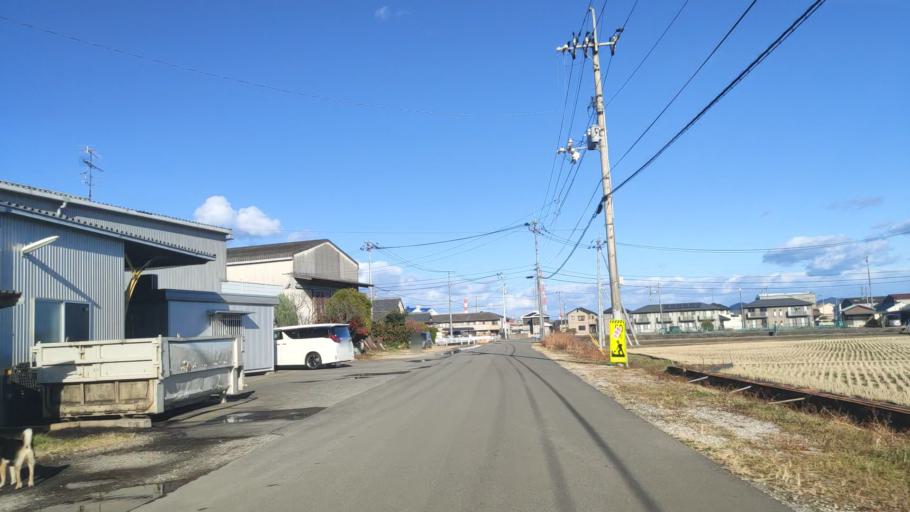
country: JP
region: Ehime
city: Saijo
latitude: 33.9216
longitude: 133.1607
